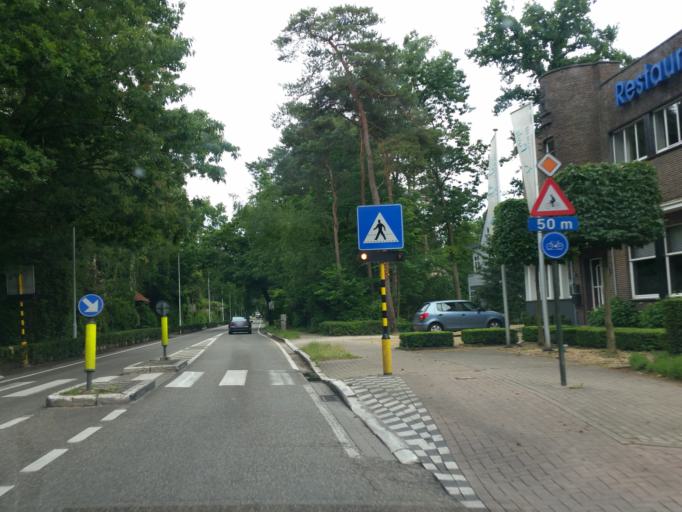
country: BE
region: Flanders
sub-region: Provincie Antwerpen
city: Schoten
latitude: 51.2666
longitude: 4.5391
